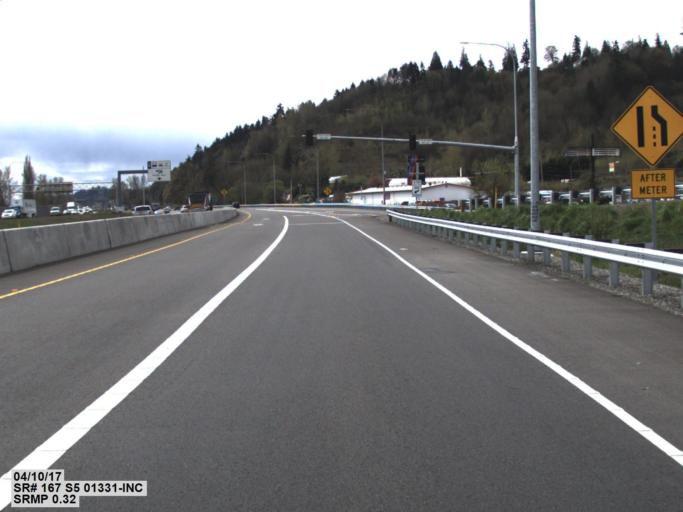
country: US
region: Washington
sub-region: Pierce County
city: Fife
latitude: 47.2391
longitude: -122.4015
